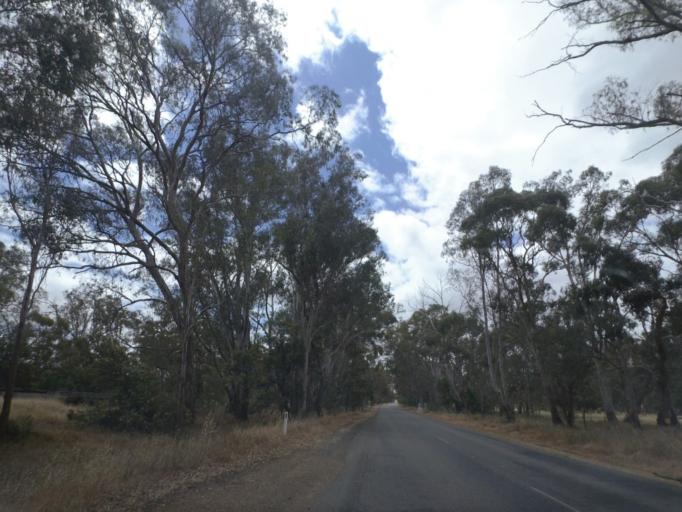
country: AU
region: Victoria
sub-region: Murrindindi
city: Kinglake West
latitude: -36.9327
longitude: 145.1805
